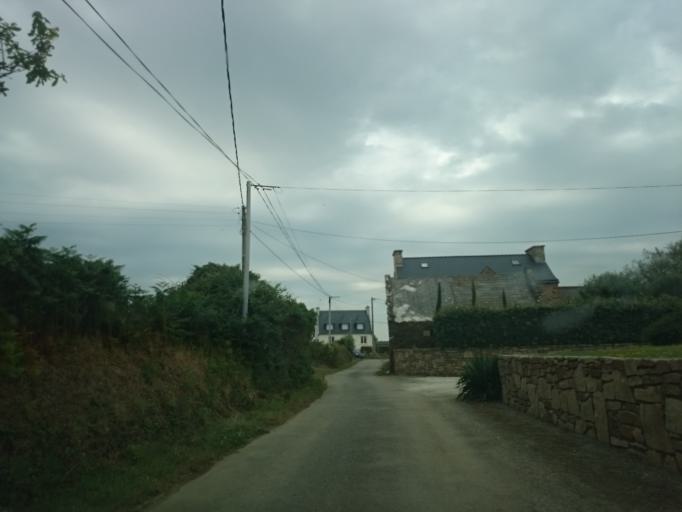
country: FR
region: Brittany
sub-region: Departement du Finistere
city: Le Conquet
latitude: 48.4026
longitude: -4.7667
